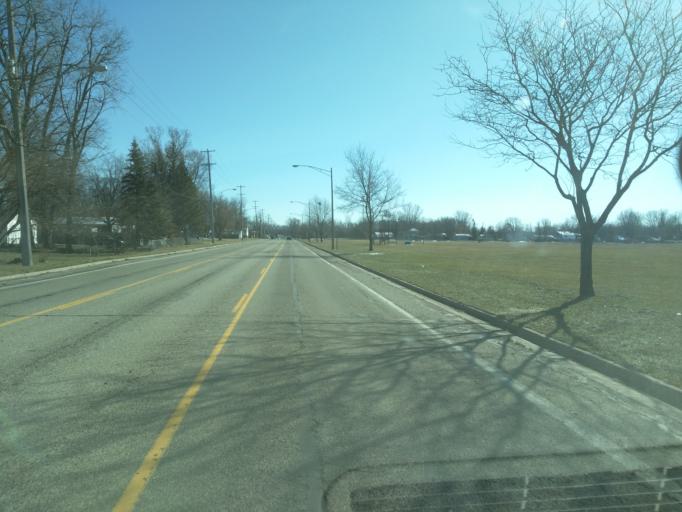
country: US
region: Michigan
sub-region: Ingham County
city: Lansing
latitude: 42.6742
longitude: -84.5873
